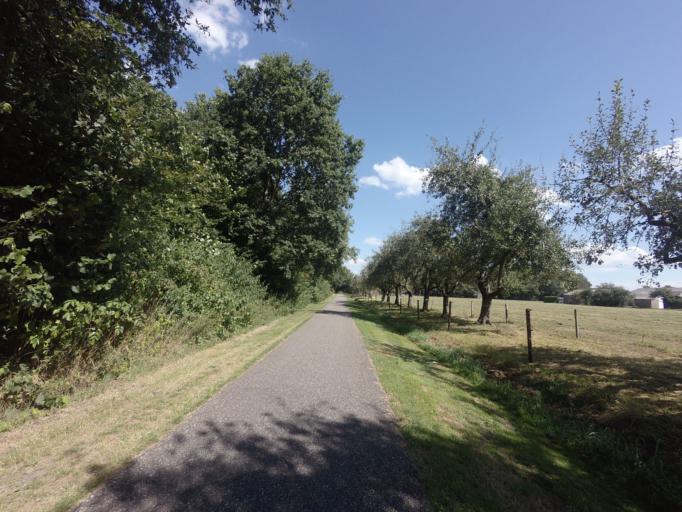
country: NL
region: Overijssel
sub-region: Gemeente Twenterand
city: Den Ham
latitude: 52.5919
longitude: 6.4584
